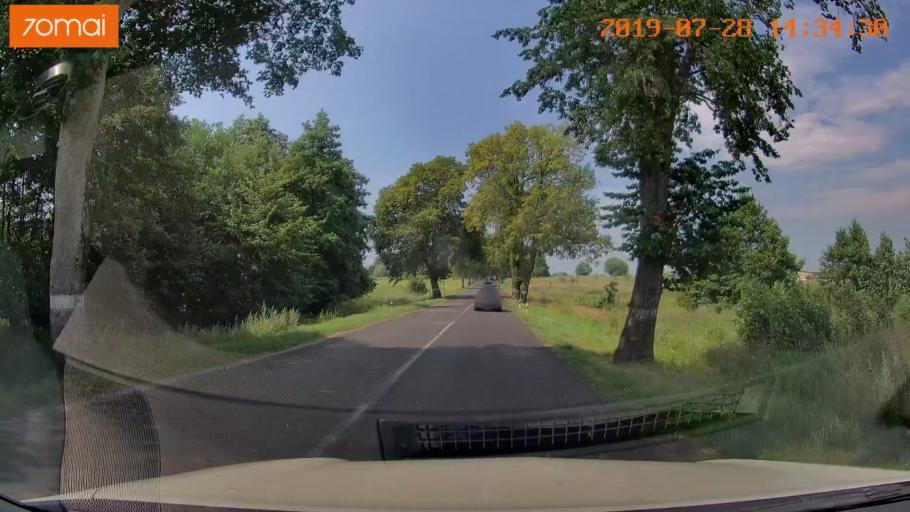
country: RU
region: Kaliningrad
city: Primorsk
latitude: 54.8256
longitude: 20.0178
